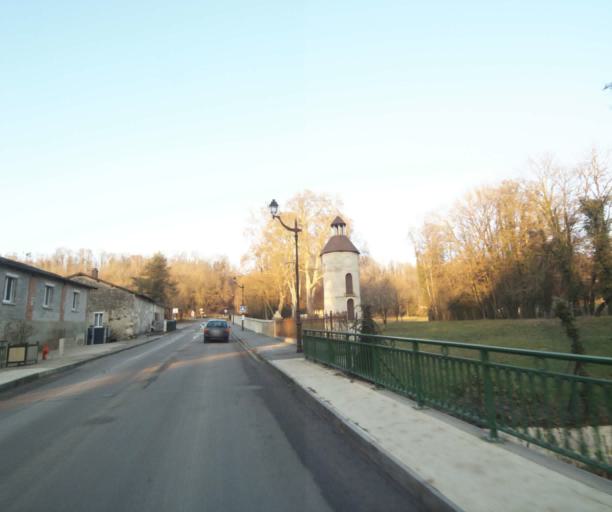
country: FR
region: Champagne-Ardenne
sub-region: Departement de la Haute-Marne
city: Bienville
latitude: 48.6097
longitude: 5.0463
